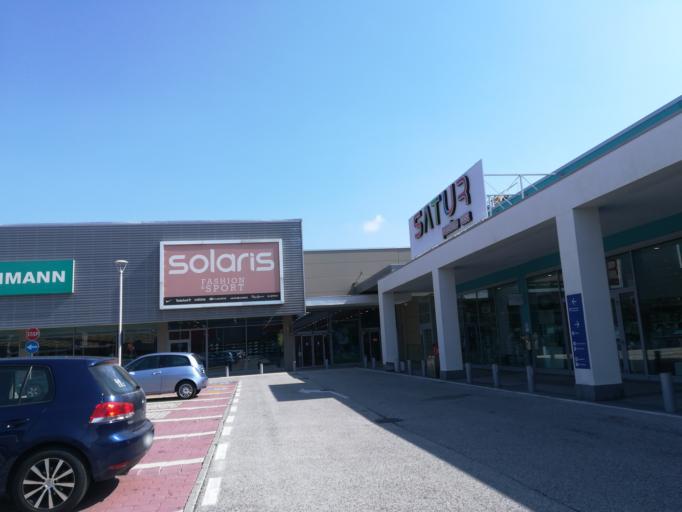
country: IT
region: The Marches
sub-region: Provincia di Macerata
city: Tolentino
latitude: 43.2171
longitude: 13.3095
